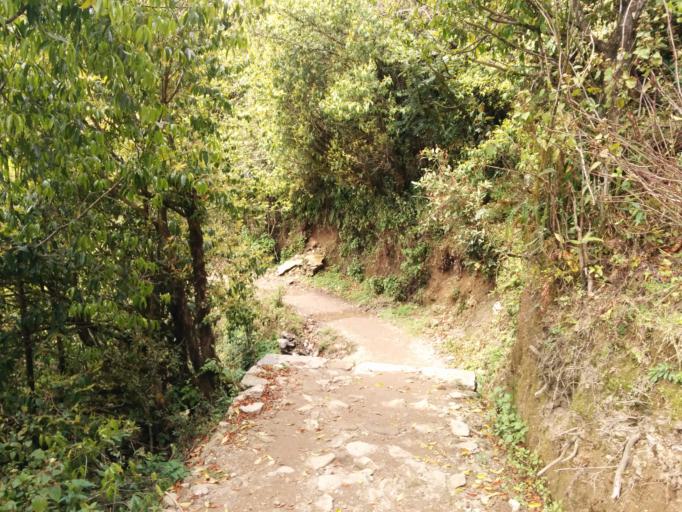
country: NP
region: Central Region
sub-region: Bagmati Zone
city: Nagarkot
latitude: 27.8220
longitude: 85.4468
